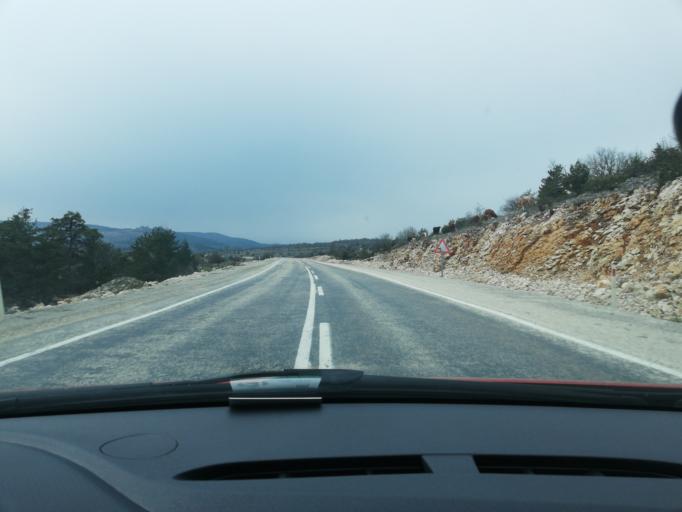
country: TR
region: Kastamonu
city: Pinarbasi
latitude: 41.5587
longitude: 33.0680
